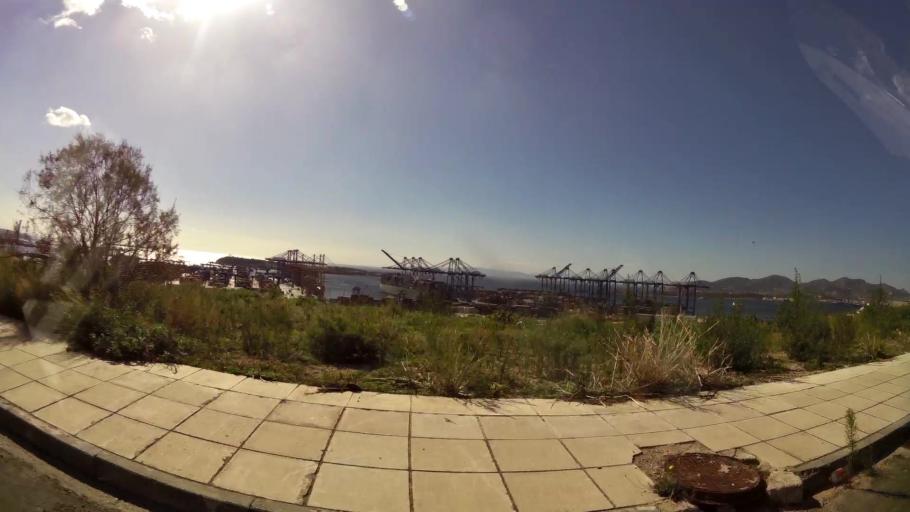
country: GR
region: Attica
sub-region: Nomos Piraios
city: Perama
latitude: 37.9641
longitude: 23.5885
